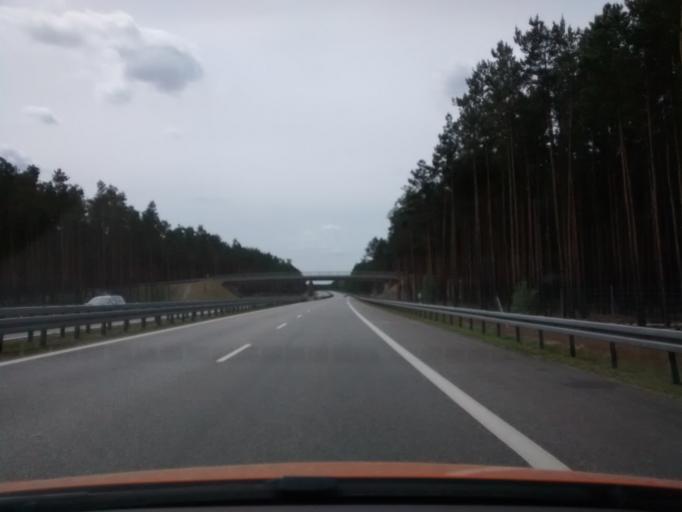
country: DE
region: Brandenburg
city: Trebbin
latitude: 52.1470
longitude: 13.2356
